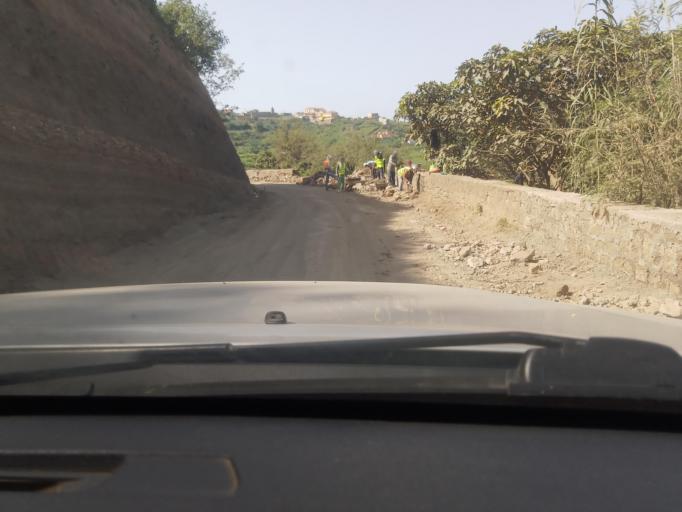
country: CV
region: Brava
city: Vila Nova Sintra
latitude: 14.8655
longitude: -24.7126
